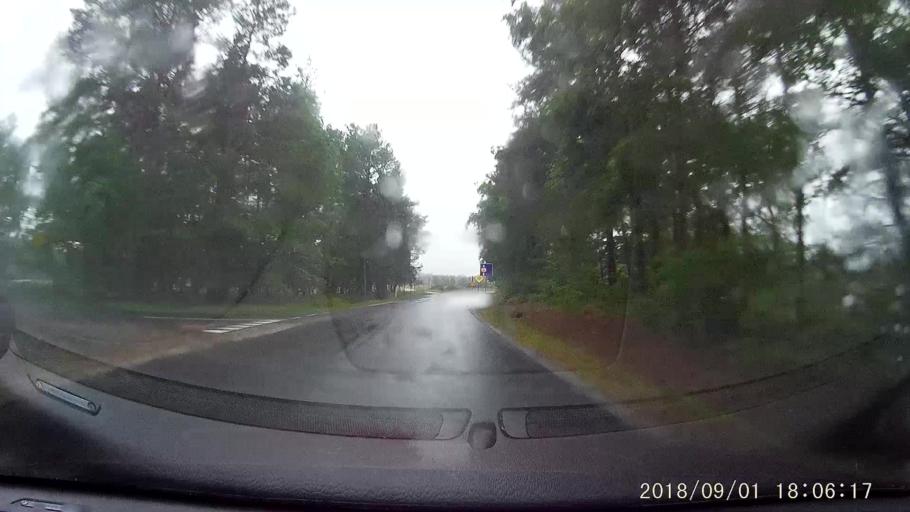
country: PL
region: Lower Silesian Voivodeship
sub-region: Powiat zgorzelecki
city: Wegliniec
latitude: 51.3553
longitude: 15.1575
